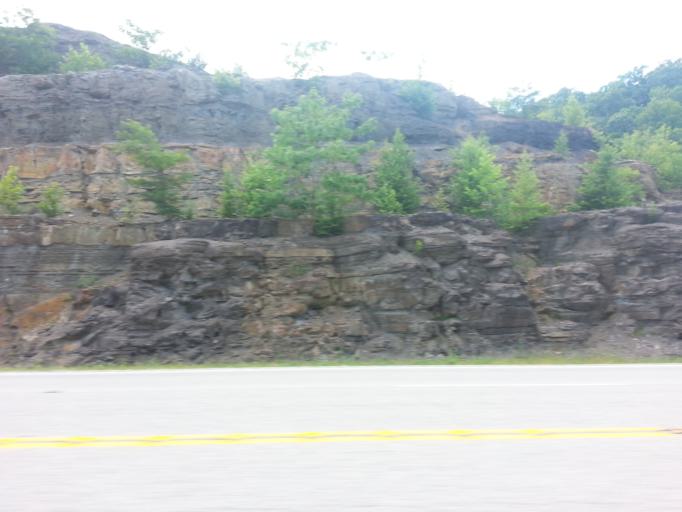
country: US
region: Kentucky
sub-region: Harlan County
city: Harlan
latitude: 36.7961
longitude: -83.2680
